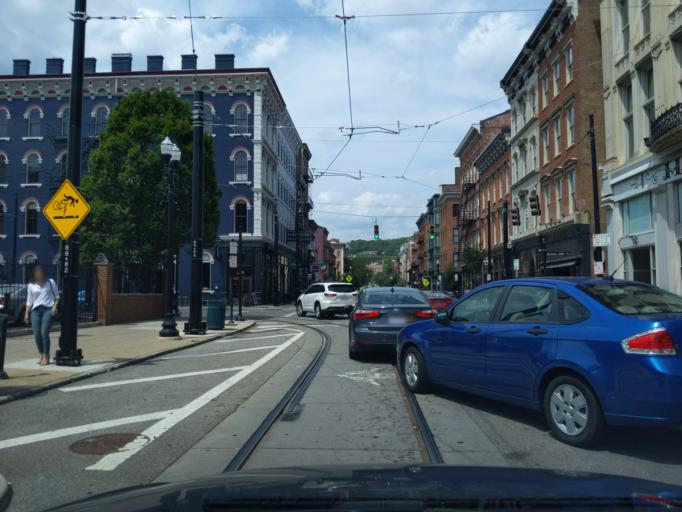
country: US
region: Kentucky
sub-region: Campbell County
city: Newport
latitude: 39.1085
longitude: -84.5114
